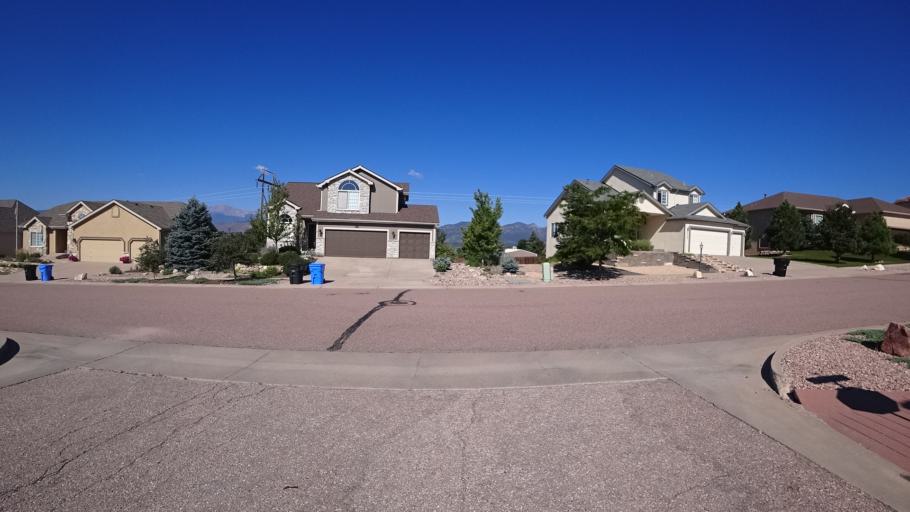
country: US
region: Colorado
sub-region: El Paso County
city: Gleneagle
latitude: 38.9750
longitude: -104.7836
